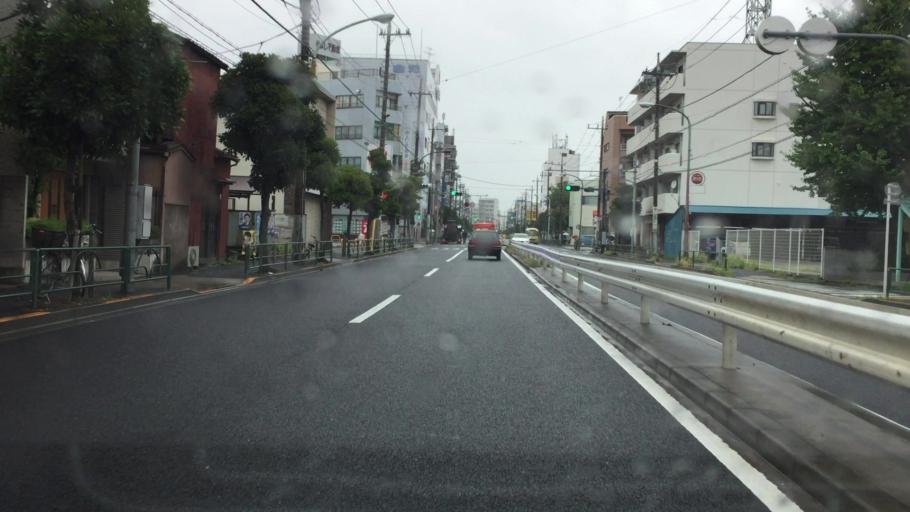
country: JP
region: Saitama
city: Soka
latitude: 35.7650
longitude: 139.7866
